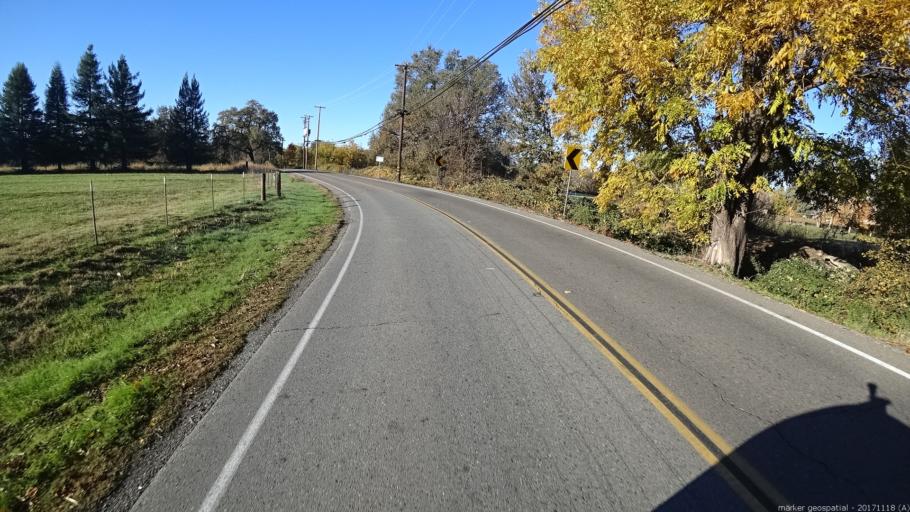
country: US
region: California
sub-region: Shasta County
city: Anderson
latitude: 40.4552
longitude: -122.2741
